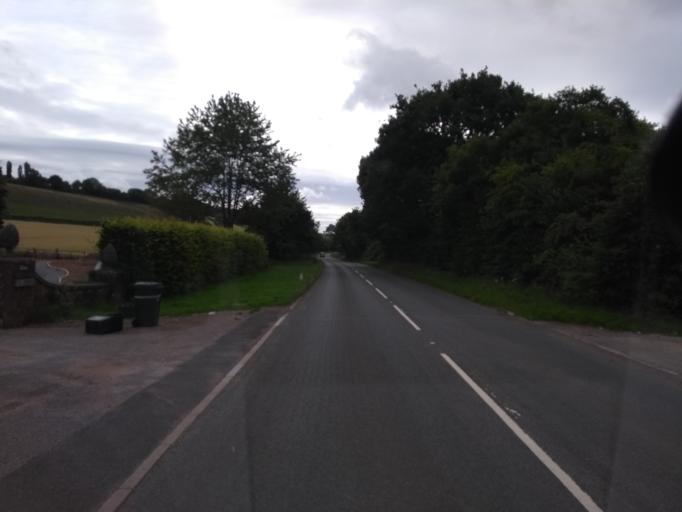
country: GB
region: England
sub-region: Somerset
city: Wiveliscombe
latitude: 51.0415
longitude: -3.3028
